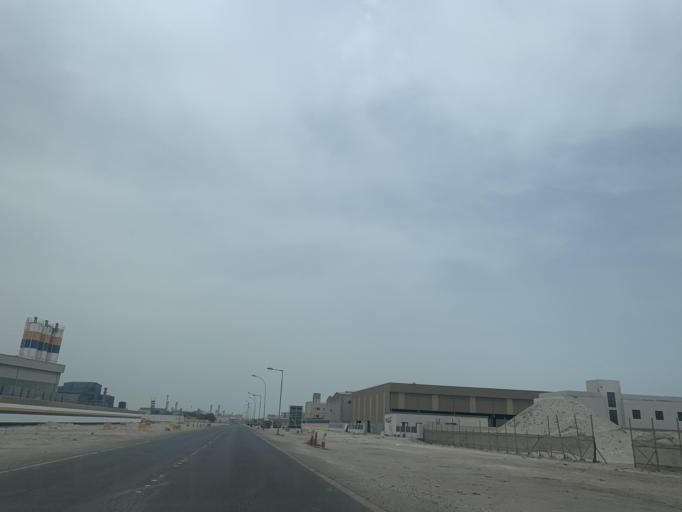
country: BH
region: Muharraq
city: Al Hadd
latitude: 26.2058
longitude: 50.6760
